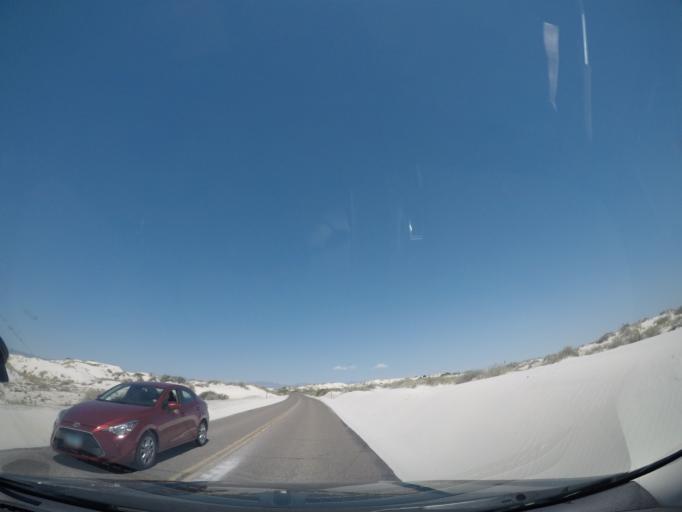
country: US
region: New Mexico
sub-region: Otero County
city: Holloman Air Force Base
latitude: 32.7960
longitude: -106.2175
